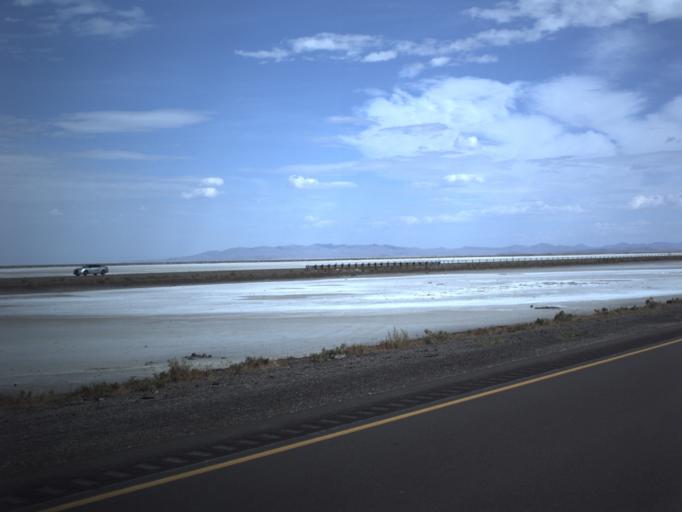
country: US
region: Utah
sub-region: Tooele County
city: Wendover
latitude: 40.7292
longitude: -113.4276
